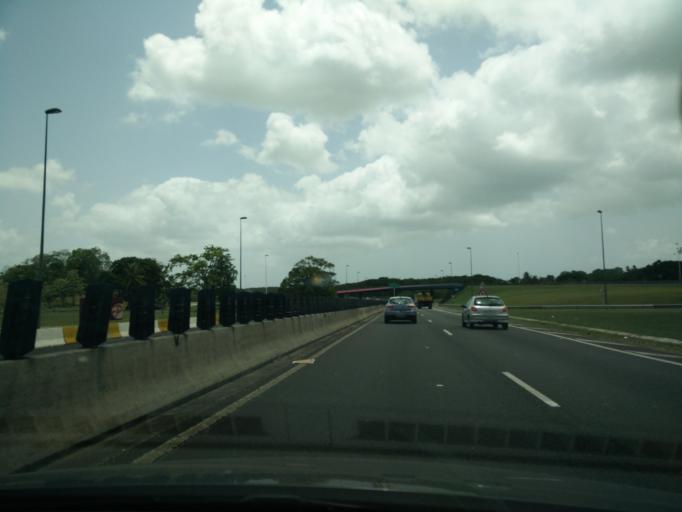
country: GP
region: Guadeloupe
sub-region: Guadeloupe
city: Les Abymes
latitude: 16.2743
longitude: -61.5184
